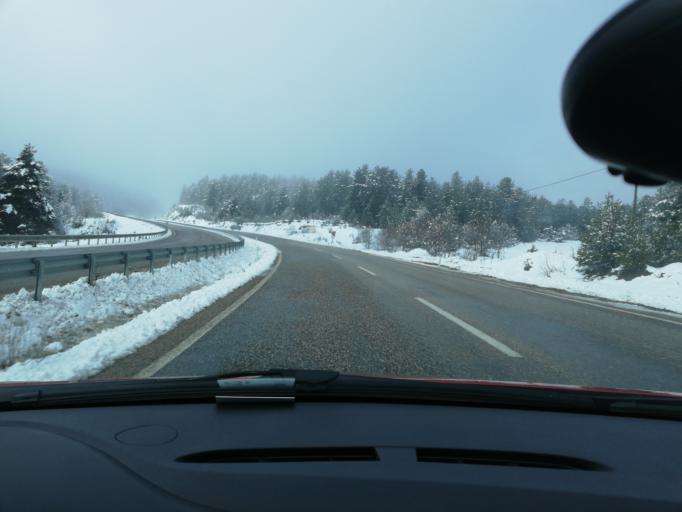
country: TR
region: Kastamonu
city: Akkaya
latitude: 41.3004
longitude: 33.5330
